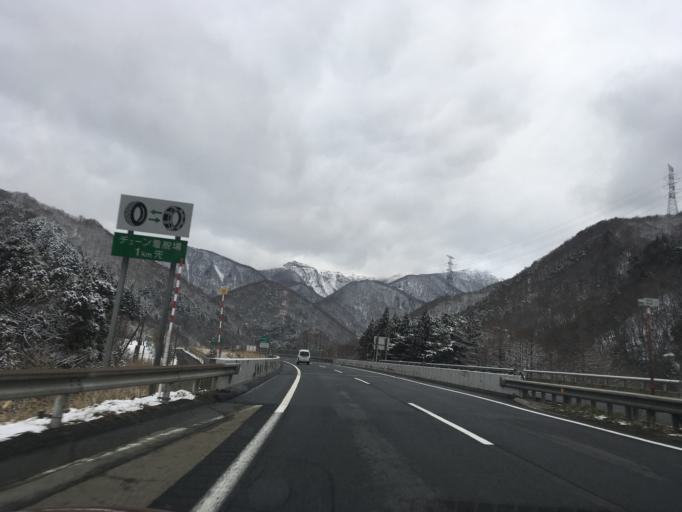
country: JP
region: Yamagata
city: Yamagata-shi
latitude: 38.2258
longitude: 140.5013
